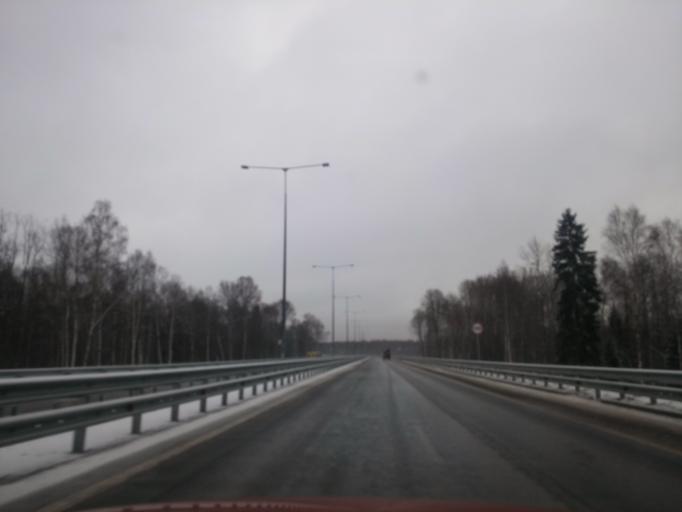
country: RU
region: Tverskaya
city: Likhoslavl'
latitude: 56.9628
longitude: 35.4765
